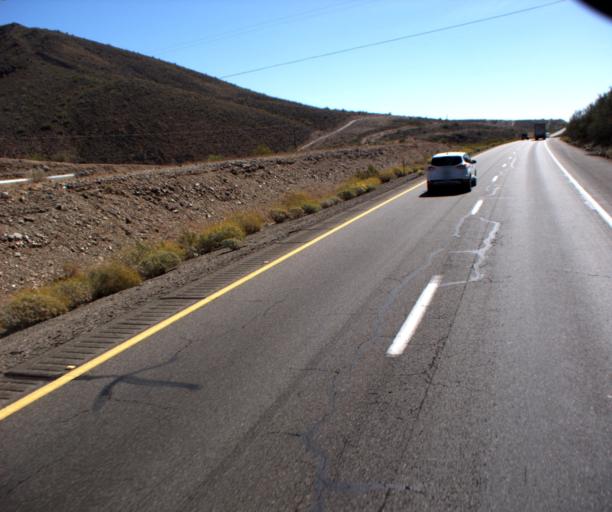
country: US
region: Arizona
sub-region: La Paz County
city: Quartzsite
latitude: 33.6748
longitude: -114.0517
